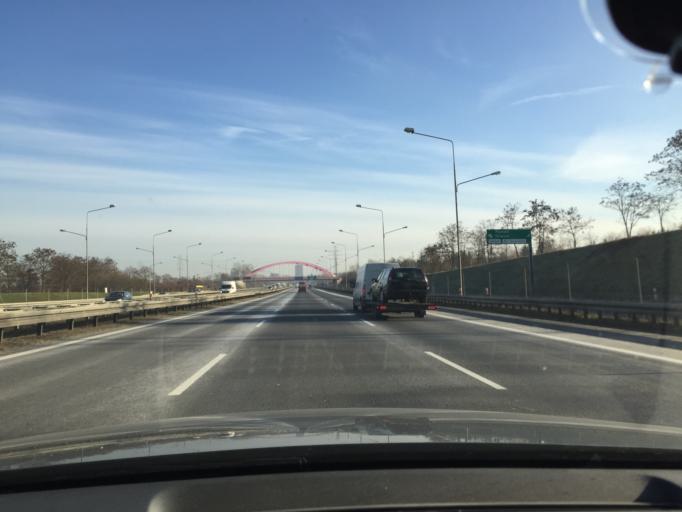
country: PL
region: Silesian Voivodeship
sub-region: Katowice
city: Katowice
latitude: 50.2531
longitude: 18.9830
